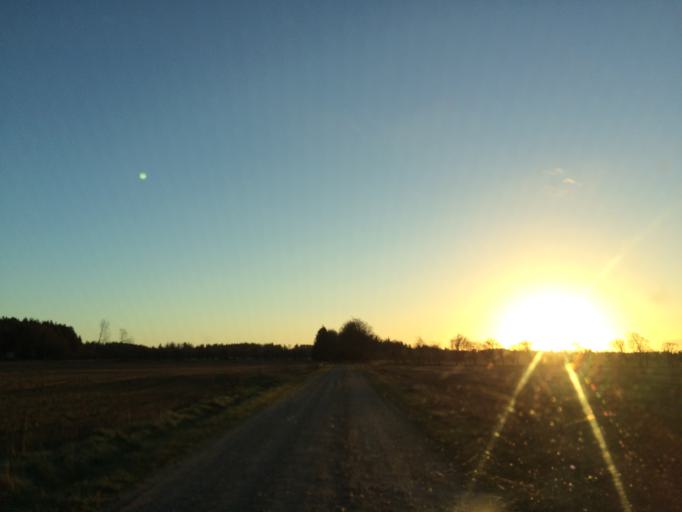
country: DK
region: Central Jutland
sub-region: Holstebro Kommune
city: Ulfborg
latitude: 56.2421
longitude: 8.4580
